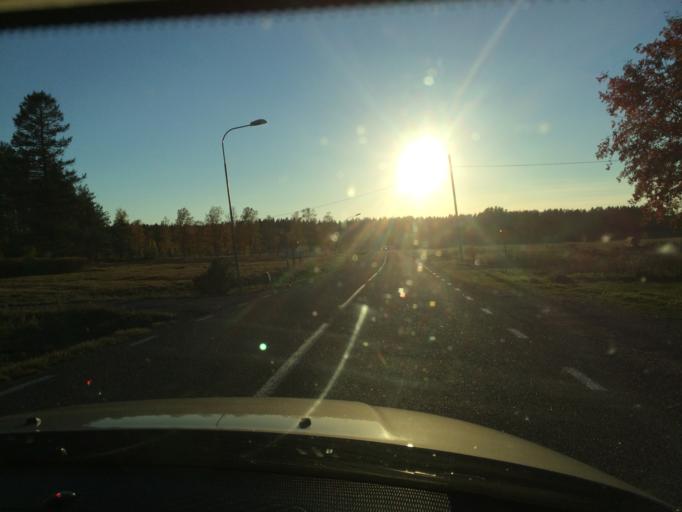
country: SE
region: Gaevleborg
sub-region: Sandvikens Kommun
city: Arsunda
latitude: 60.4523
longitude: 16.7041
